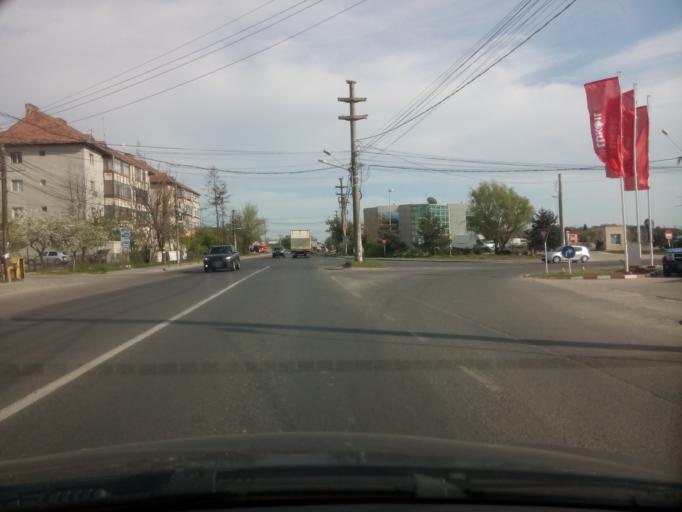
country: RO
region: Ilfov
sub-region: Comuna Mogosoaia
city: Mogosoaia
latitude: 44.5230
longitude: 26.0066
